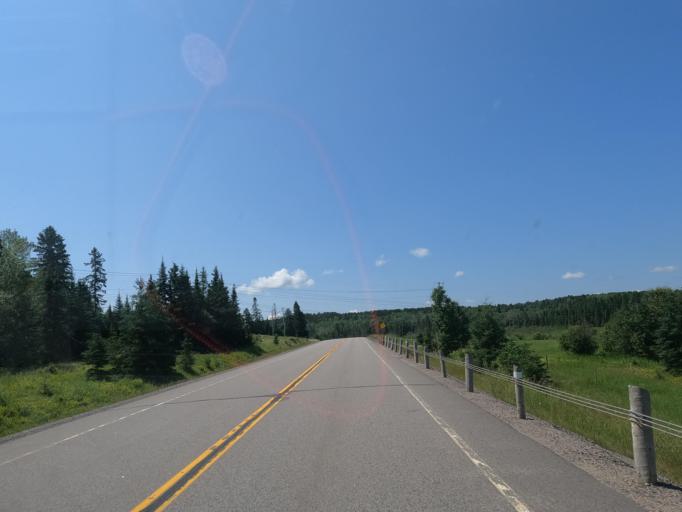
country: CA
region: Ontario
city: Dryden
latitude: 49.8622
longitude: -93.3619
